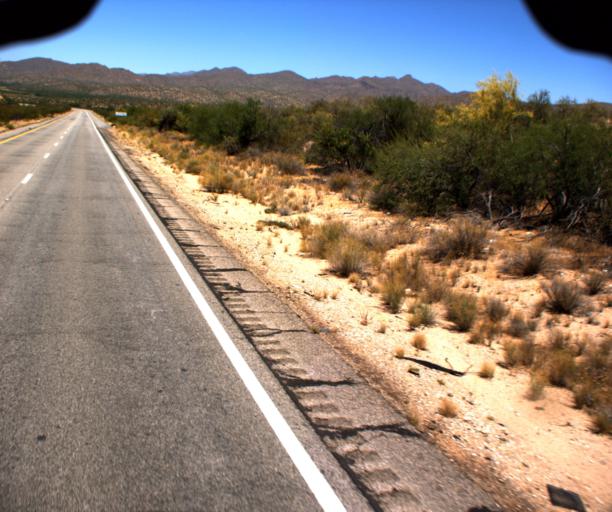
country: US
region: Arizona
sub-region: Yavapai County
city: Bagdad
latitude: 34.3626
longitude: -113.1740
